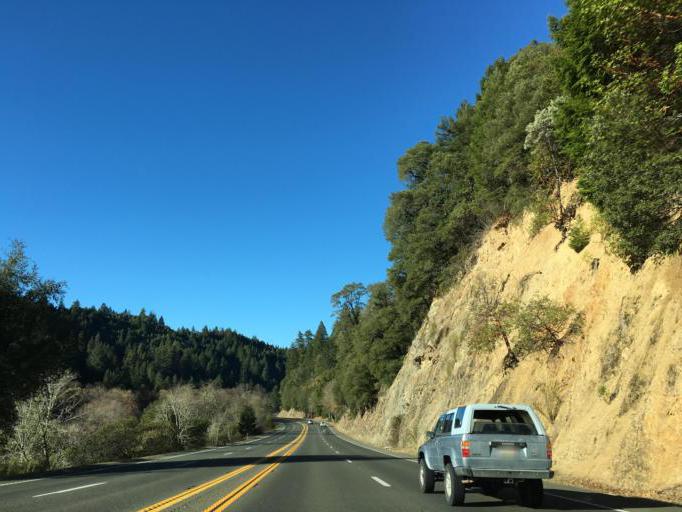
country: US
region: California
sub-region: Mendocino County
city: Brooktrails
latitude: 39.5253
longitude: -123.3998
